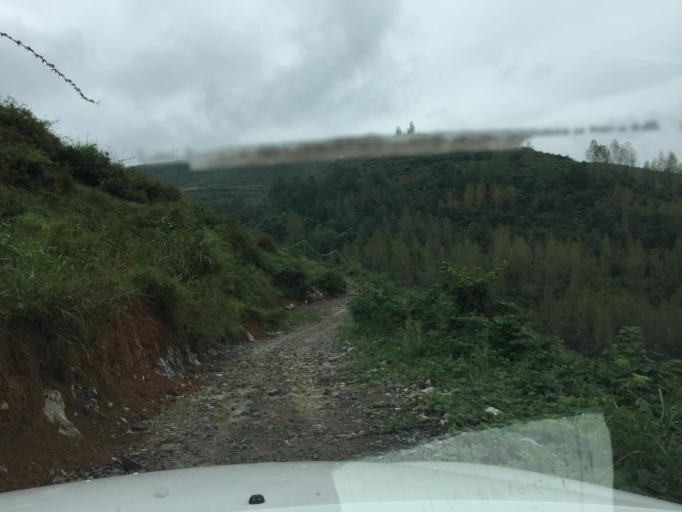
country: CN
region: Guizhou Sheng
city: Yantang
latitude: 28.2020
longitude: 108.0836
